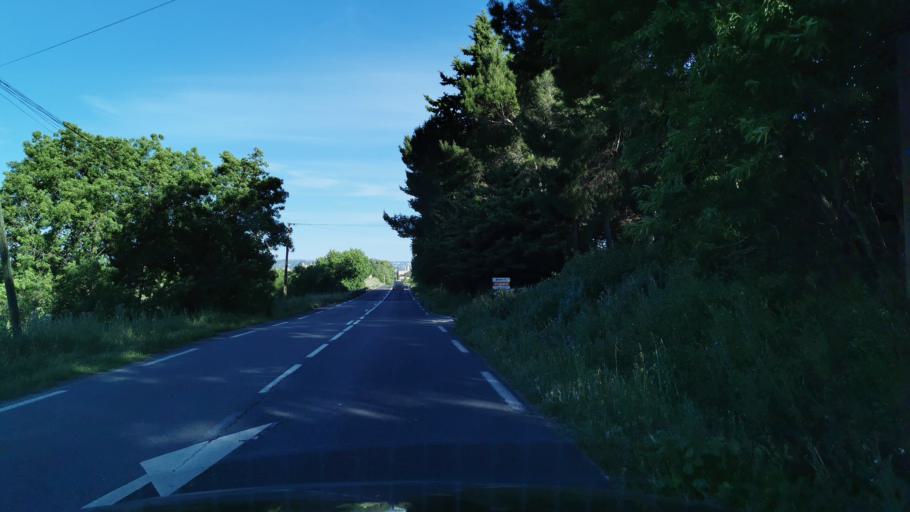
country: FR
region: Languedoc-Roussillon
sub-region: Departement de l'Aude
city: Moussan
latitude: 43.2023
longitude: 2.9661
